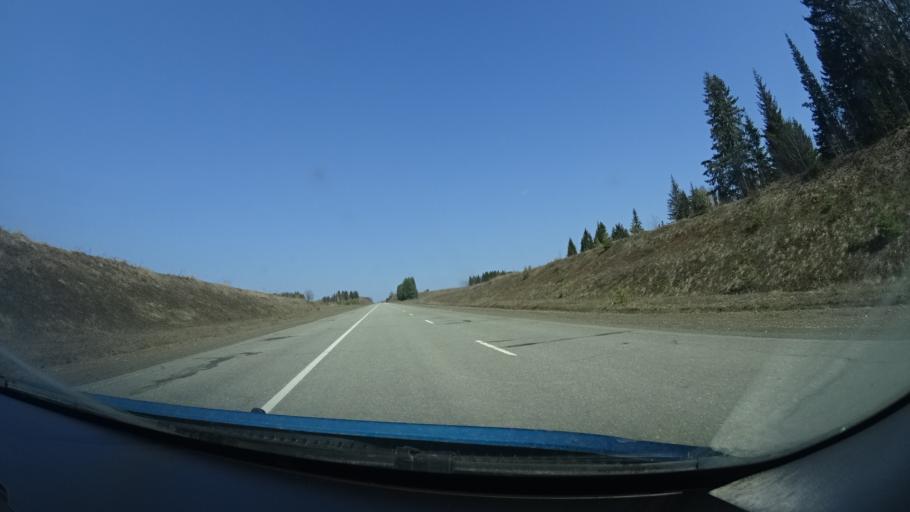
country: RU
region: Perm
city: Yugo-Kamskiy
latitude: 57.4870
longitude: 55.6830
